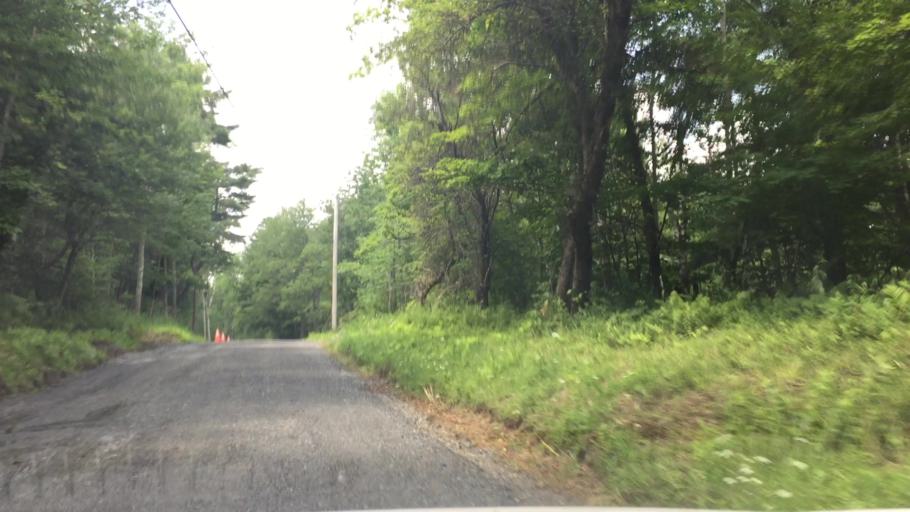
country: US
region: Massachusetts
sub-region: Berkshire County
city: Lee
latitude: 42.2740
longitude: -73.1822
